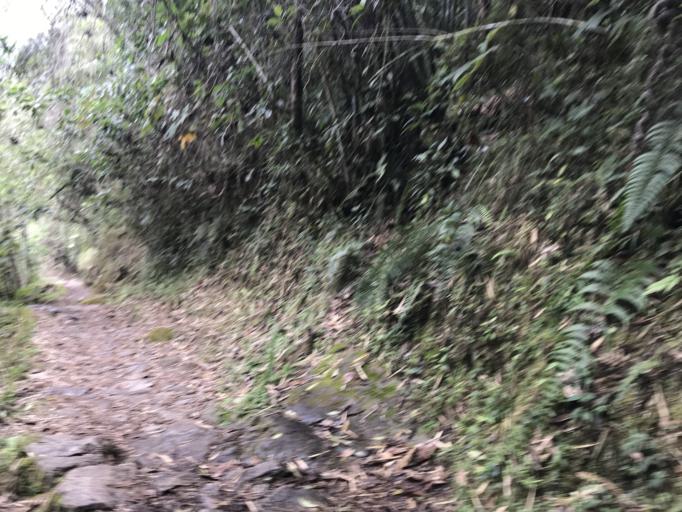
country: PE
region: Cusco
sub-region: Provincia de La Convencion
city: Santa Teresa
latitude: -13.1746
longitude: -72.5358
